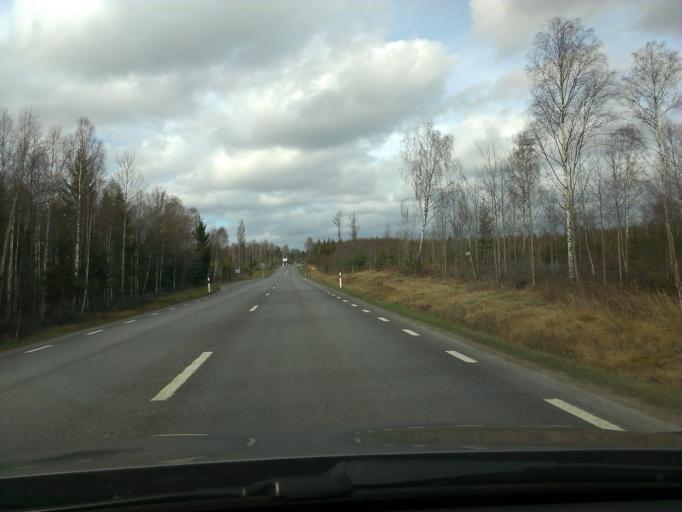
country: SE
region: Kronoberg
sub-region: Vaxjo Kommun
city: Gemla
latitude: 56.8316
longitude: 14.6970
